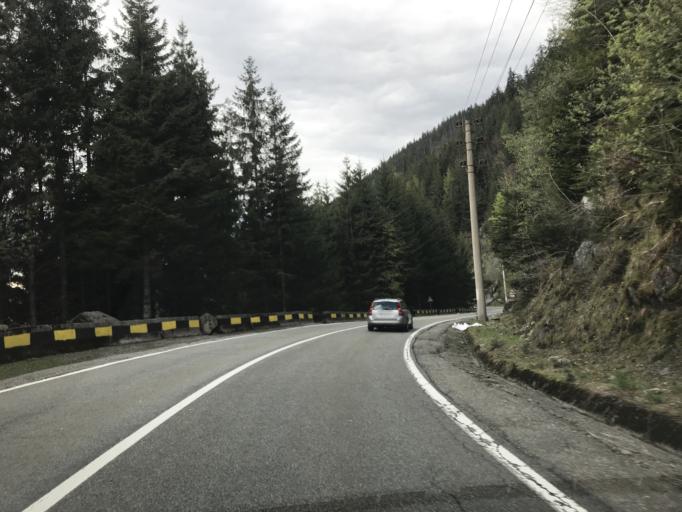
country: RO
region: Sibiu
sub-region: Comuna Cartisoara
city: Cartisoara
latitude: 45.6471
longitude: 24.6052
